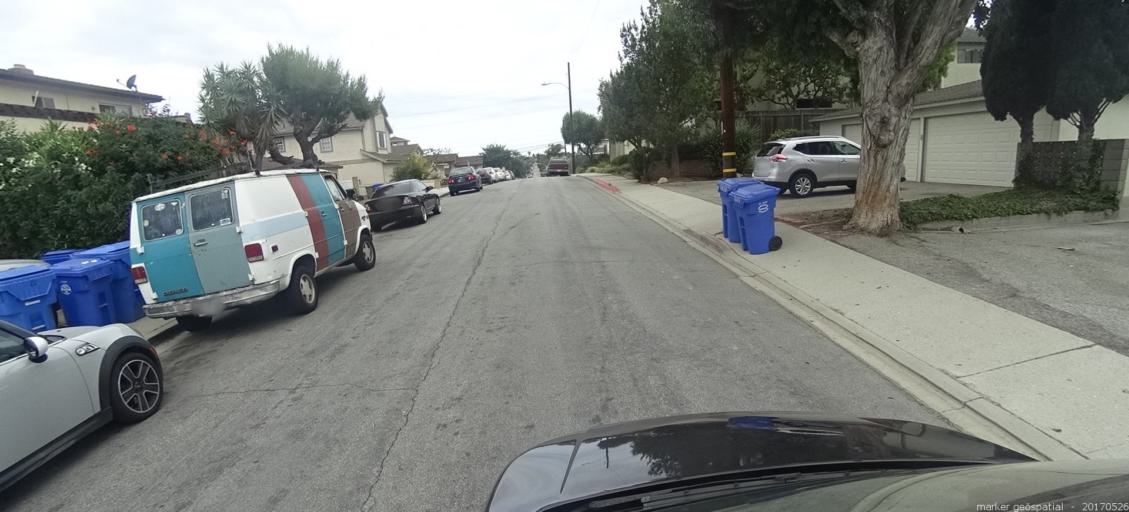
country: US
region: California
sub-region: Los Angeles County
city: Lawndale
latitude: 33.8748
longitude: -118.3631
